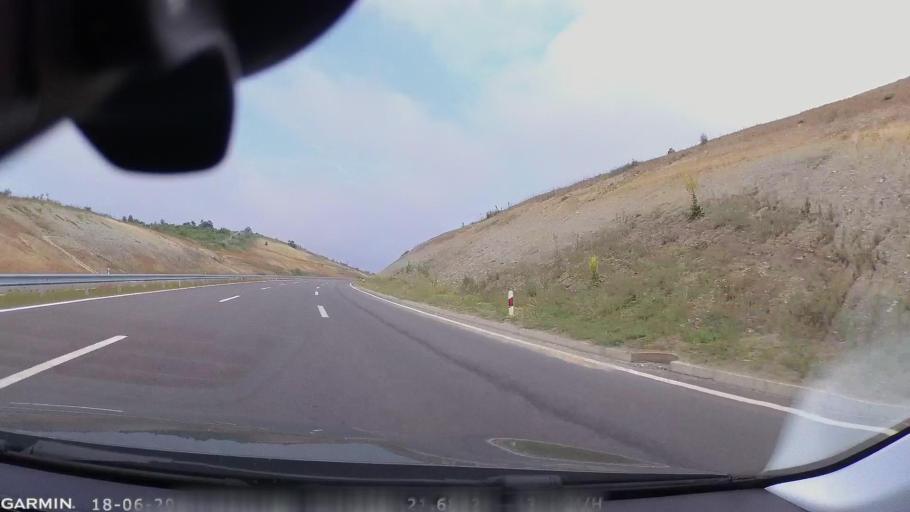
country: MK
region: Petrovec
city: Sredno Konjare
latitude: 41.9455
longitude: 21.7826
